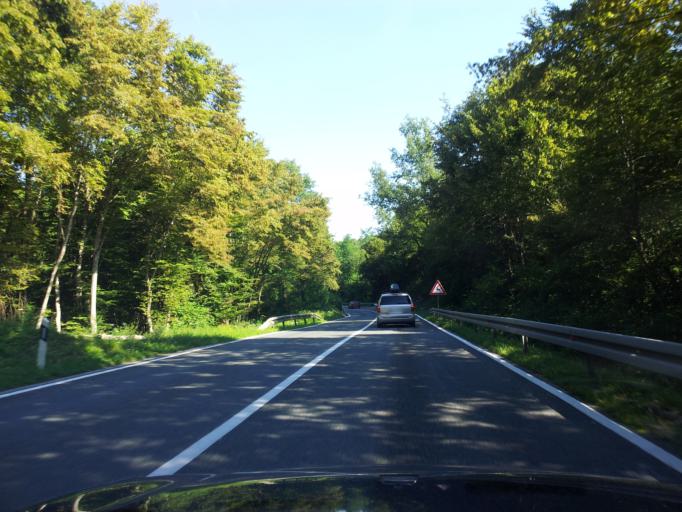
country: HR
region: Karlovacka
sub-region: Grad Karlovac
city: Slunj
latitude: 45.1957
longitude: 15.5552
